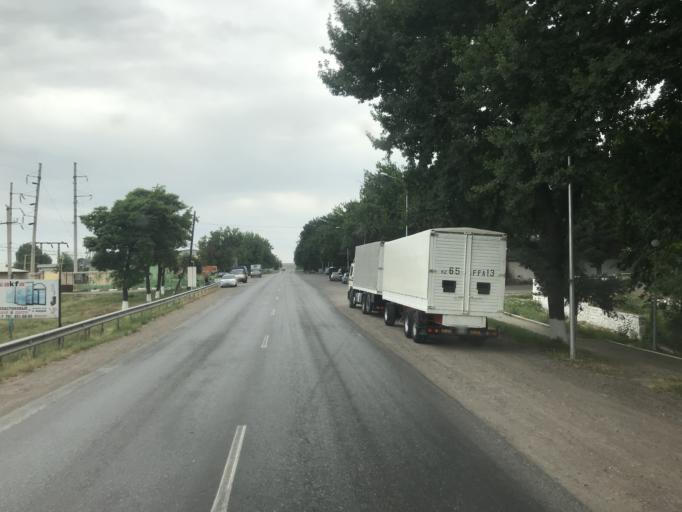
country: KZ
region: Ongtustik Qazaqstan
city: Saryaghash
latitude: 41.4908
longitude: 69.2776
